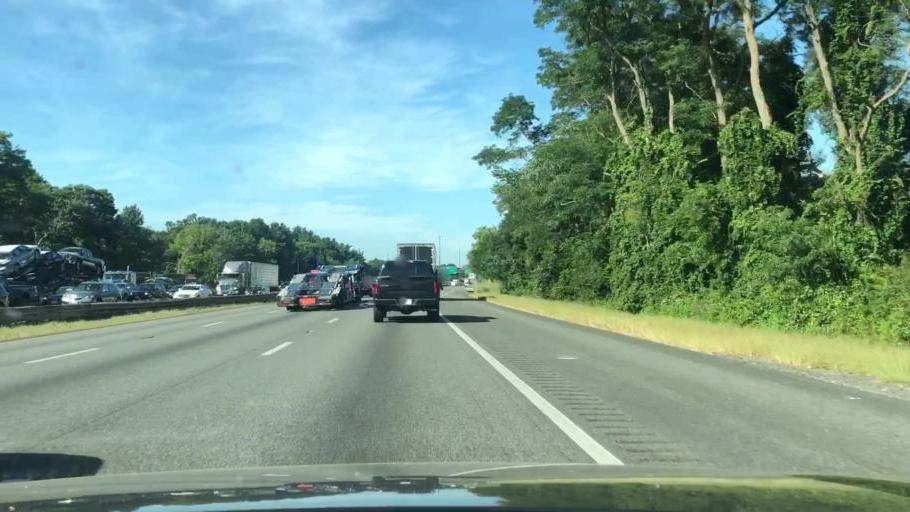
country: US
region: Massachusetts
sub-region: Middlesex County
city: Lowell
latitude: 42.6116
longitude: -71.3100
